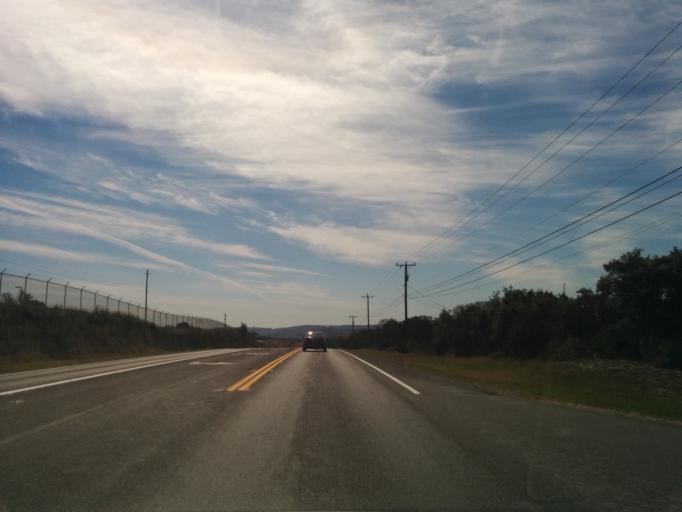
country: US
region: Texas
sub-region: Bexar County
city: Scenic Oaks
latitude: 29.6956
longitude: -98.6316
